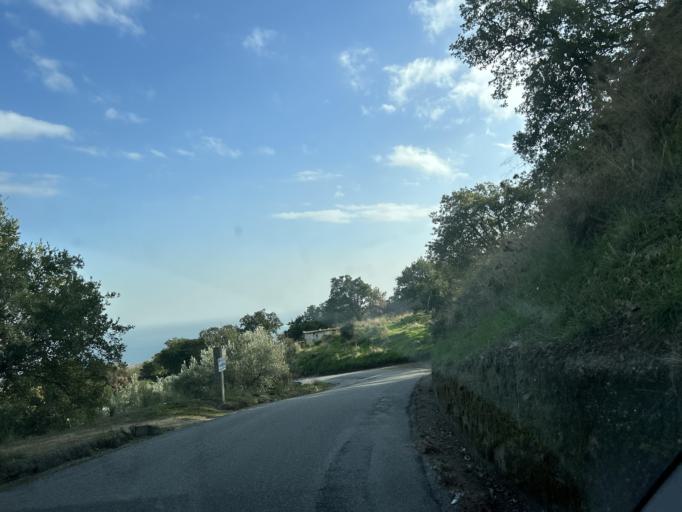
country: IT
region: Calabria
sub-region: Provincia di Catanzaro
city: Montepaone
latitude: 38.7168
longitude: 16.5110
